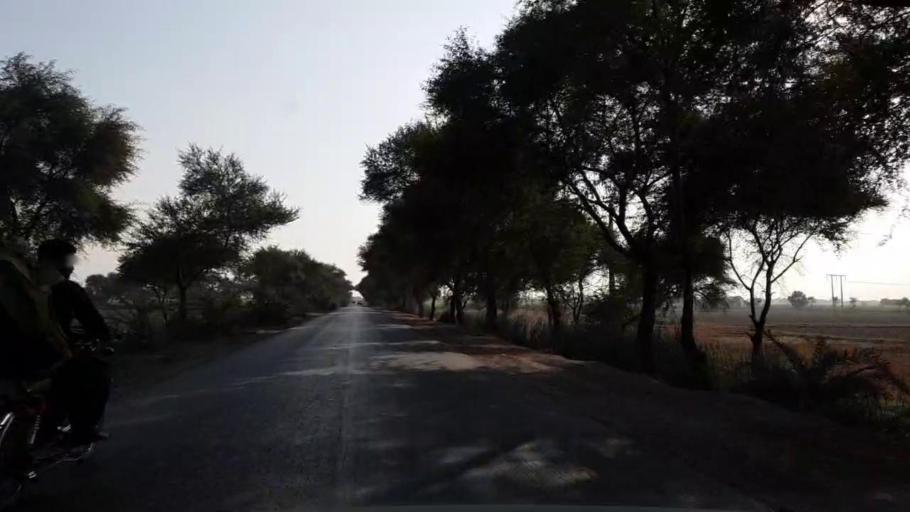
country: PK
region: Sindh
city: Bulri
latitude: 24.8750
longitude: 68.3399
